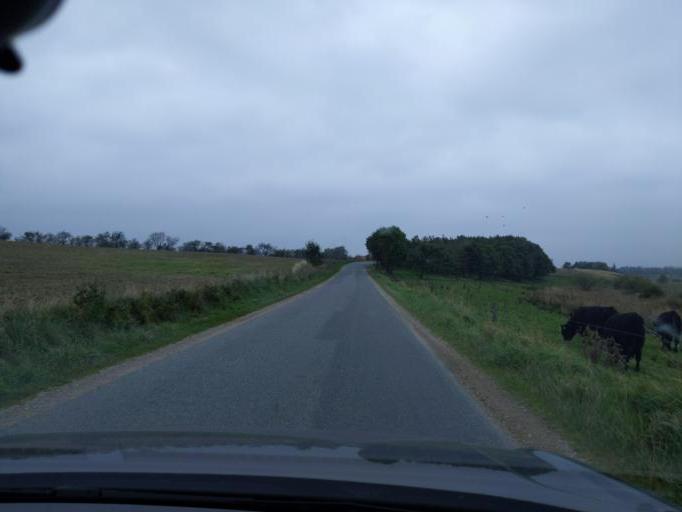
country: DK
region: Central Jutland
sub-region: Viborg Kommune
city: Stoholm
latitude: 56.4955
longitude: 9.2459
